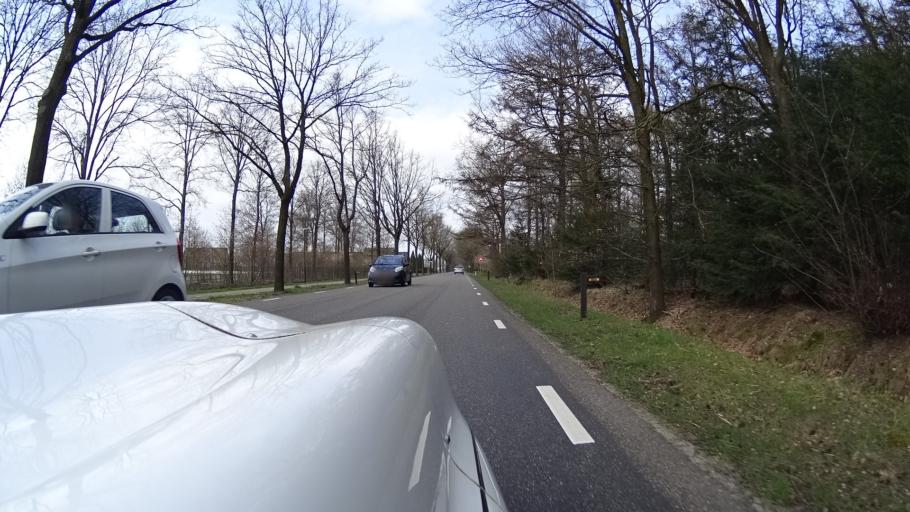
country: NL
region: North Brabant
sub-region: Gemeente Veghel
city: Keldonk
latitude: 51.5481
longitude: 5.5639
